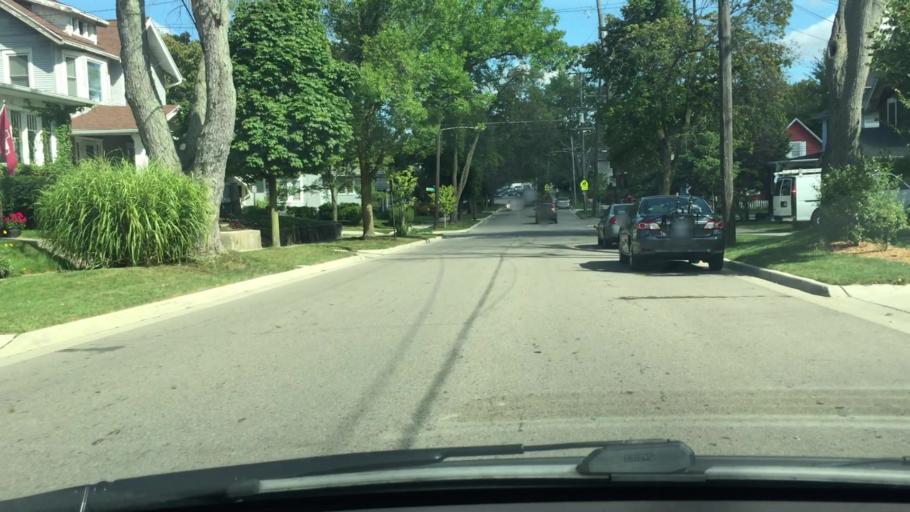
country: US
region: Michigan
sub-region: Kent County
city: East Grand Rapids
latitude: 42.9596
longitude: -85.6358
